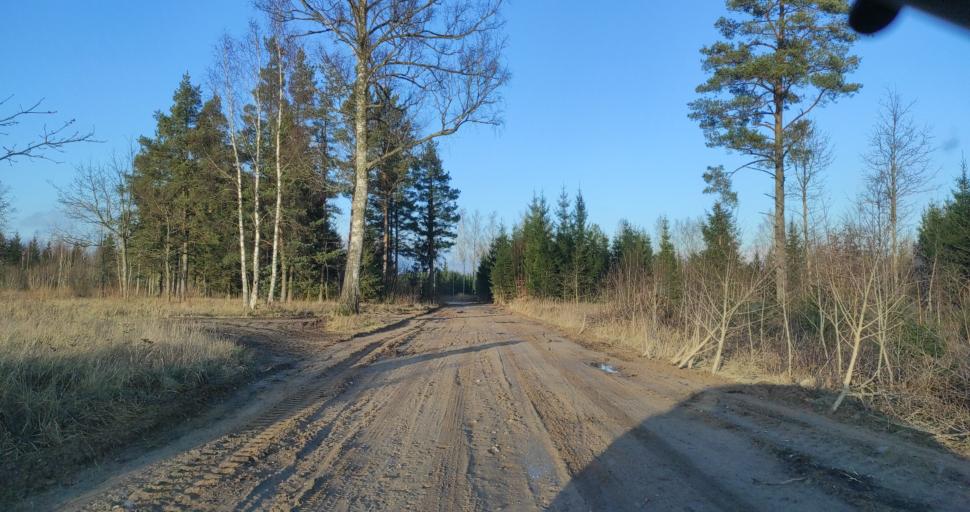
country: LV
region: Kuldigas Rajons
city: Kuldiga
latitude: 57.0535
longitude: 21.8671
